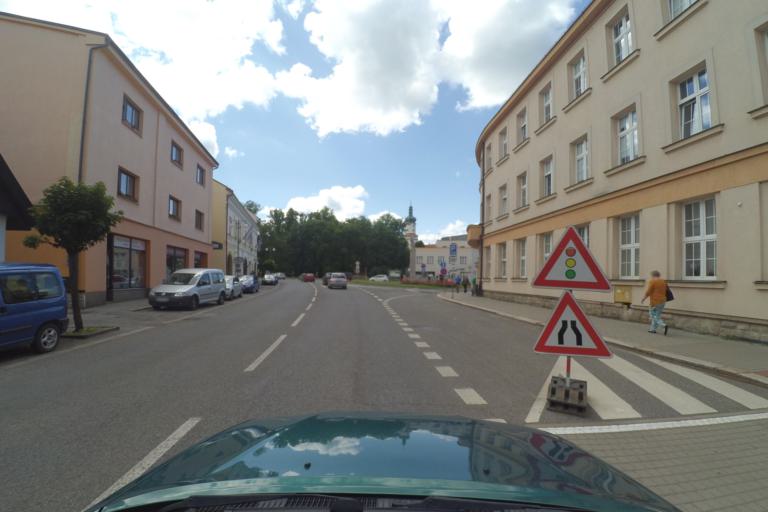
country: CZ
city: Nove Mesto nad Metuji
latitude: 50.3462
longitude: 16.1502
